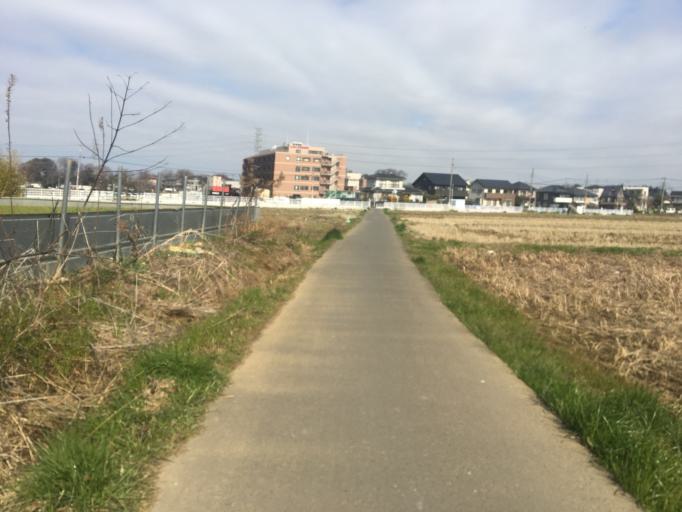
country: JP
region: Saitama
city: Shiki
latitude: 35.8395
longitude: 139.5715
